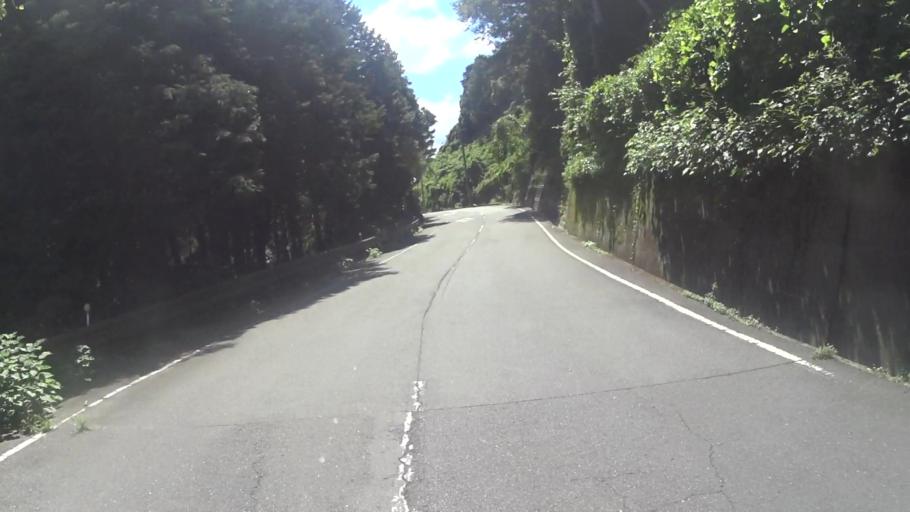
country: JP
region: Nara
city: Nara-shi
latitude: 34.7395
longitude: 135.8822
